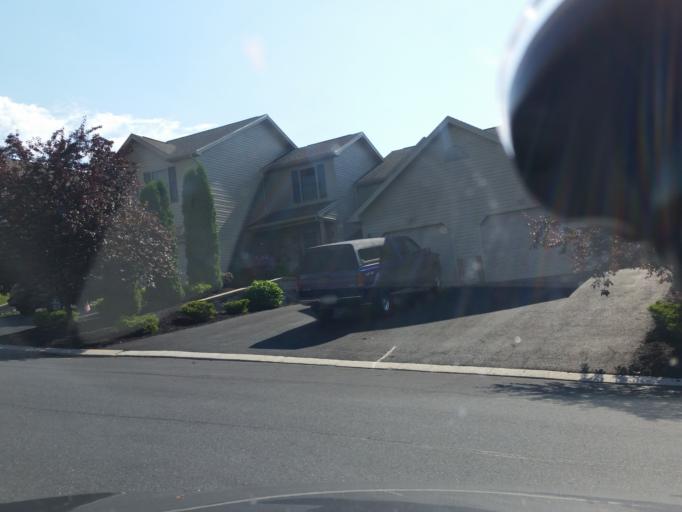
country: US
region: Pennsylvania
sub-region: Perry County
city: Marysville
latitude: 40.3337
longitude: -76.9385
